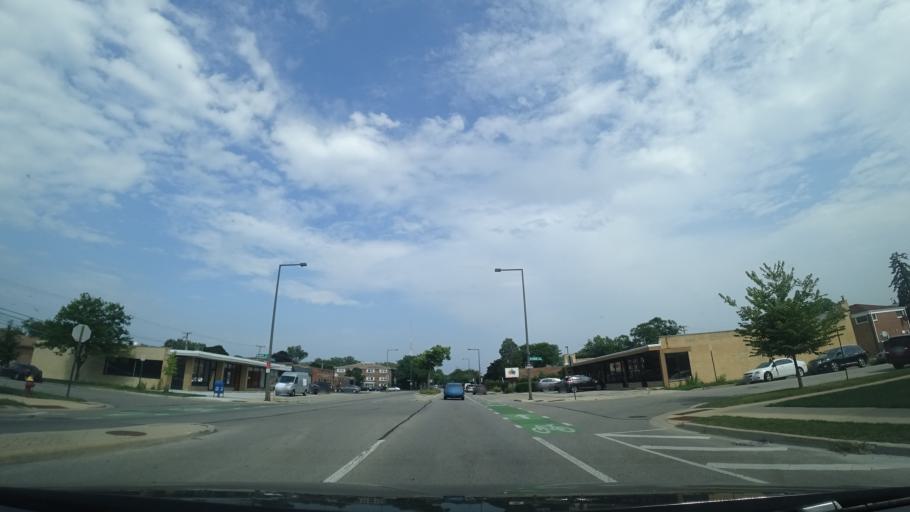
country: US
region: Illinois
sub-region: Cook County
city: Skokie
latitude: 42.0336
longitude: -87.7138
